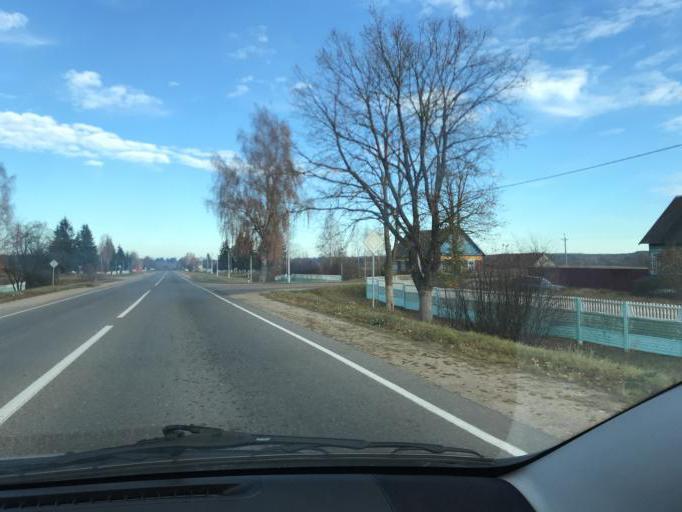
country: BY
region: Vitebsk
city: Haradok
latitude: 55.4869
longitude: 29.9676
